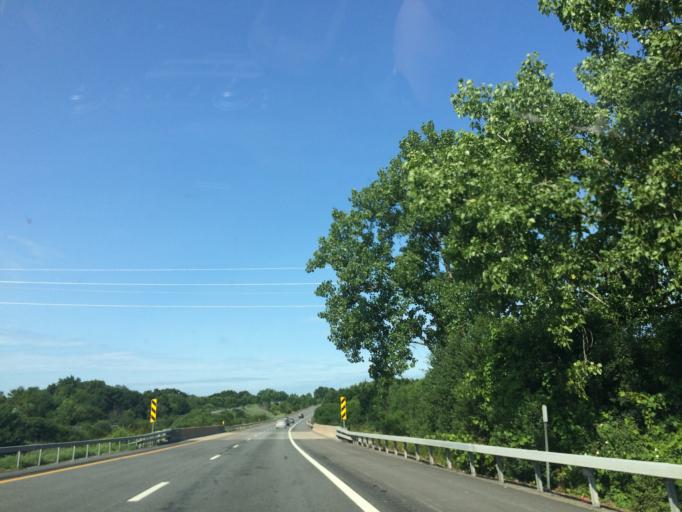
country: US
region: New York
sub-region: Orange County
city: Maybrook
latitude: 41.5023
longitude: -74.2315
